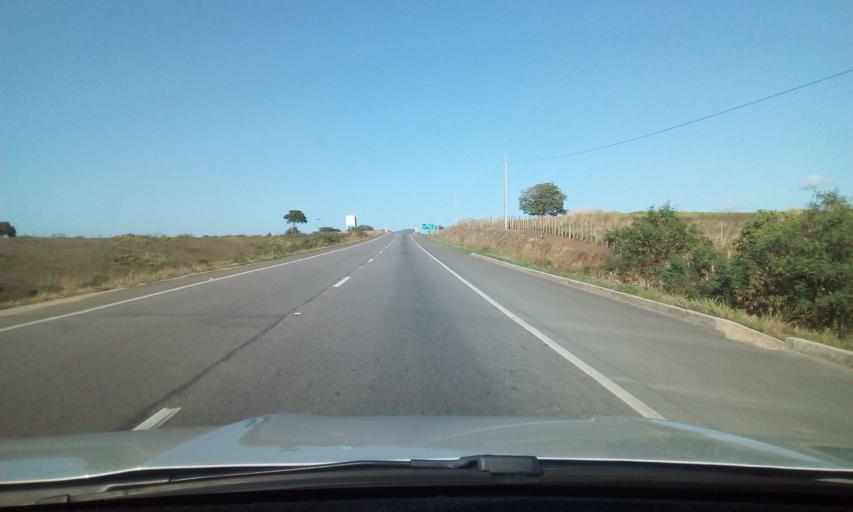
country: BR
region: Paraiba
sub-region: Gurinhem
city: Gurinhem
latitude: -7.1637
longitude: -35.3496
